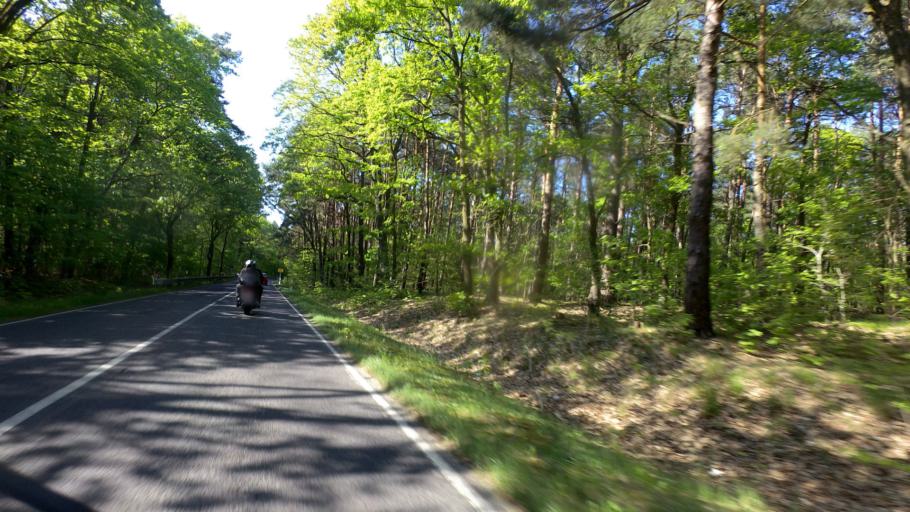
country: DE
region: Brandenburg
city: Bestensee
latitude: 52.2281
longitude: 13.6713
